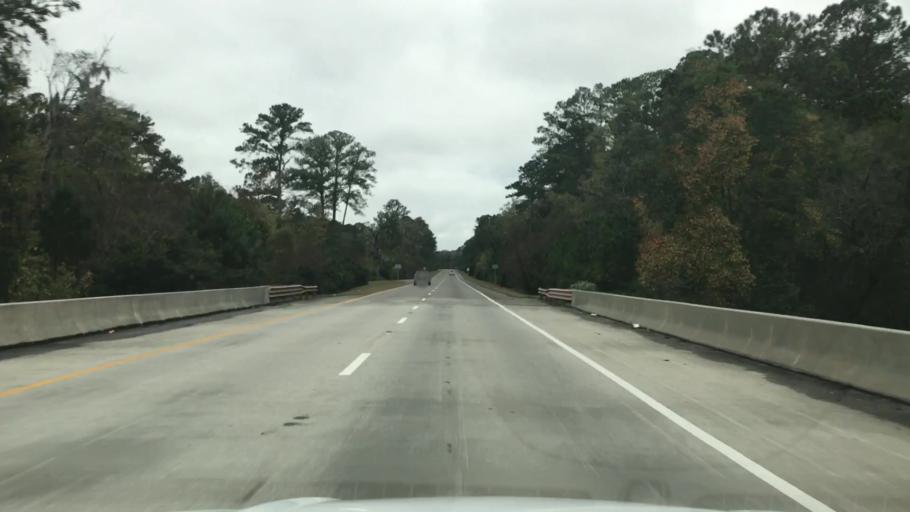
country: US
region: South Carolina
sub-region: Hampton County
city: Yemassee
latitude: 32.6478
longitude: -80.6979
